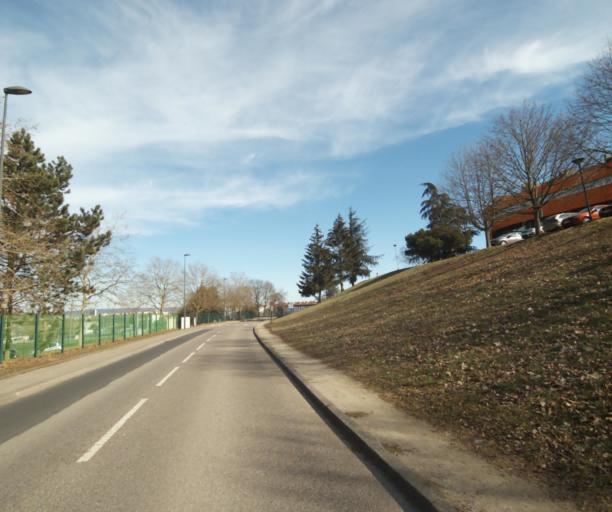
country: FR
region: Lorraine
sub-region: Departement de Meurthe-et-Moselle
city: Villers-les-Nancy
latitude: 48.6667
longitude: 6.1574
